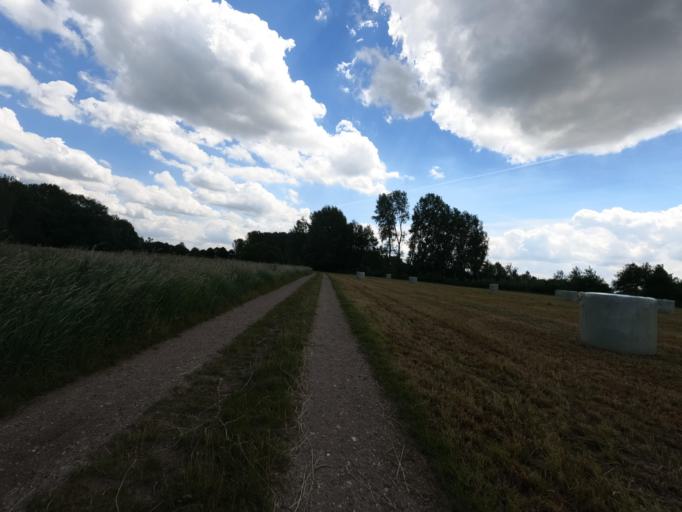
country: DE
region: North Rhine-Westphalia
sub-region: Regierungsbezirk Koln
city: Wassenberg
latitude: 51.0815
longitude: 6.1525
